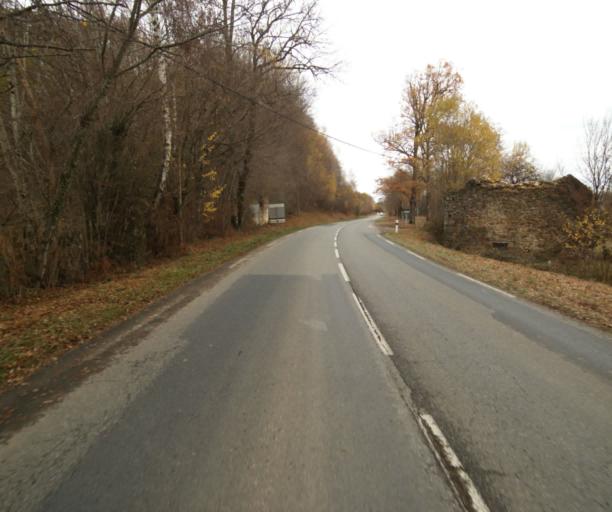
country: FR
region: Limousin
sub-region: Departement de la Correze
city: Sainte-Fortunade
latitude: 45.1852
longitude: 1.7623
